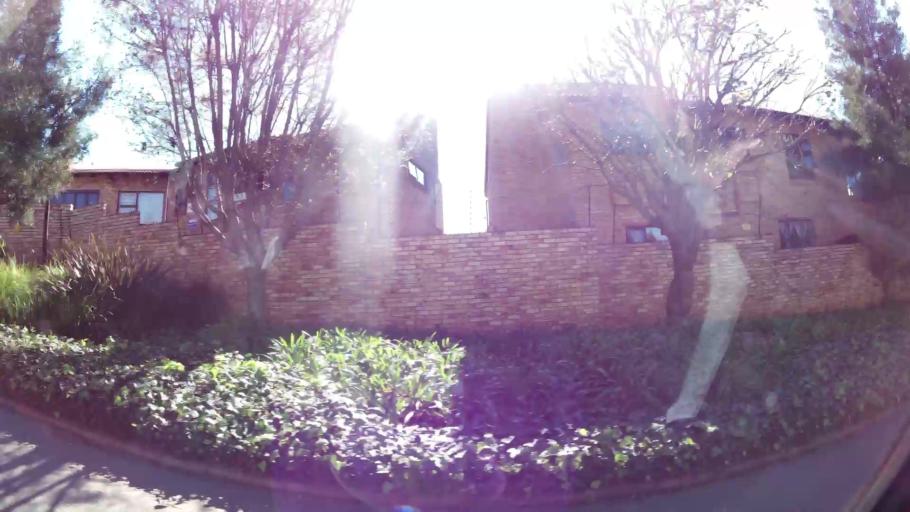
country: ZA
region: Gauteng
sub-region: City of Johannesburg Metropolitan Municipality
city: Roodepoort
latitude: -26.1188
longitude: 27.8608
